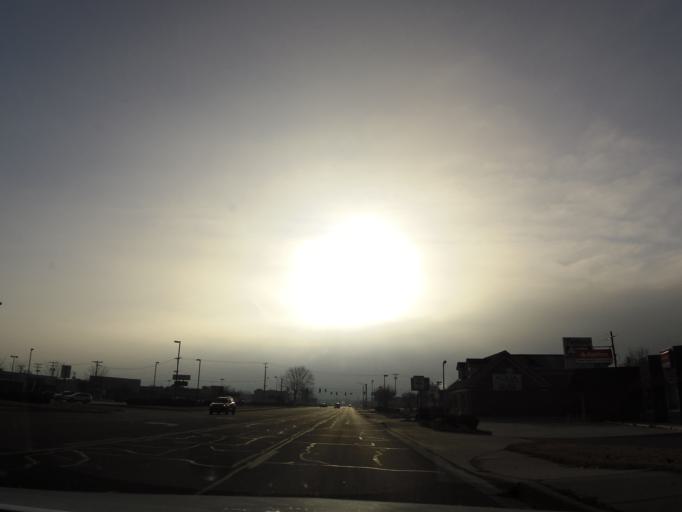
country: US
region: Indiana
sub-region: Bartholomew County
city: Columbus
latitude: 39.2220
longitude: -85.8899
